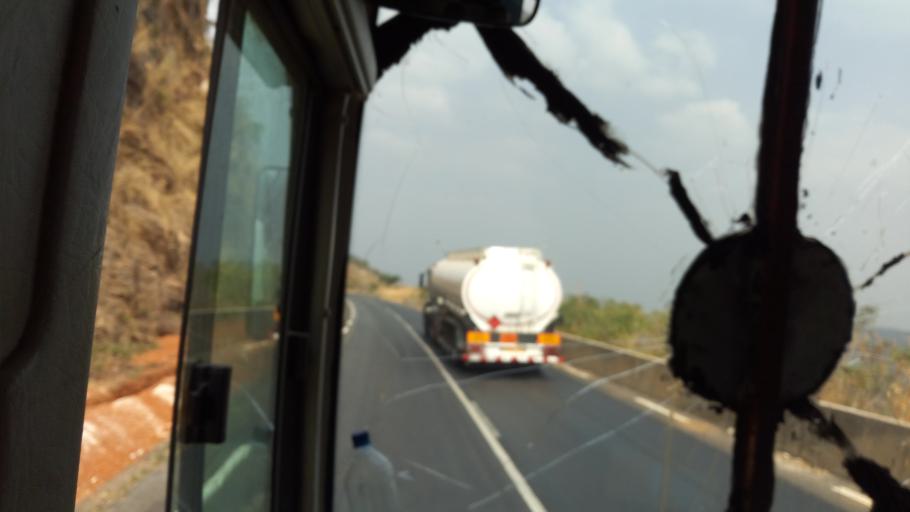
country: TG
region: Kara
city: Bafilo
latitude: 9.2529
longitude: 1.2197
